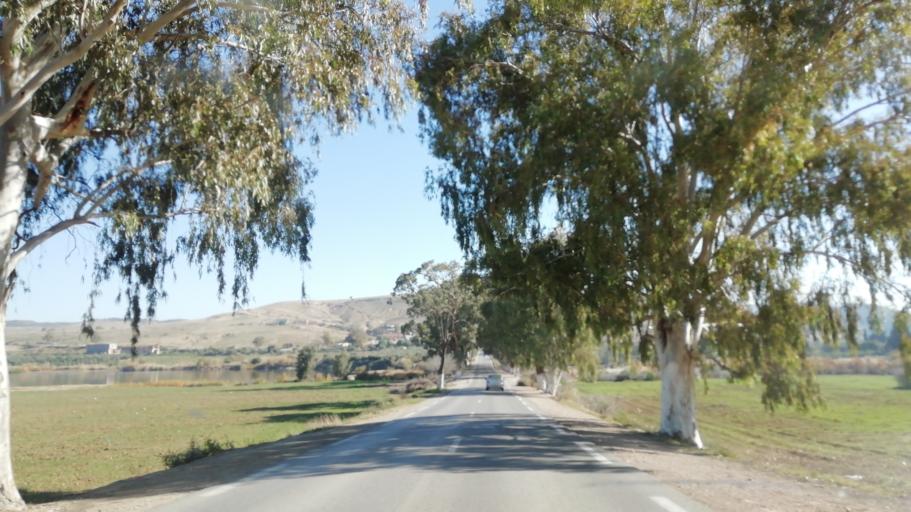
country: DZ
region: Tlemcen
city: Nedroma
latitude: 34.8271
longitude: -1.6576
